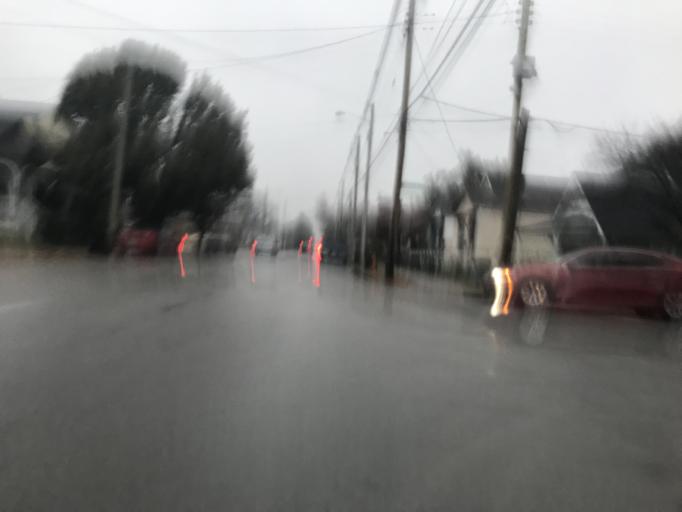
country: US
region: Kentucky
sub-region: Jefferson County
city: Louisville
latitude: 38.2429
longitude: -85.7399
